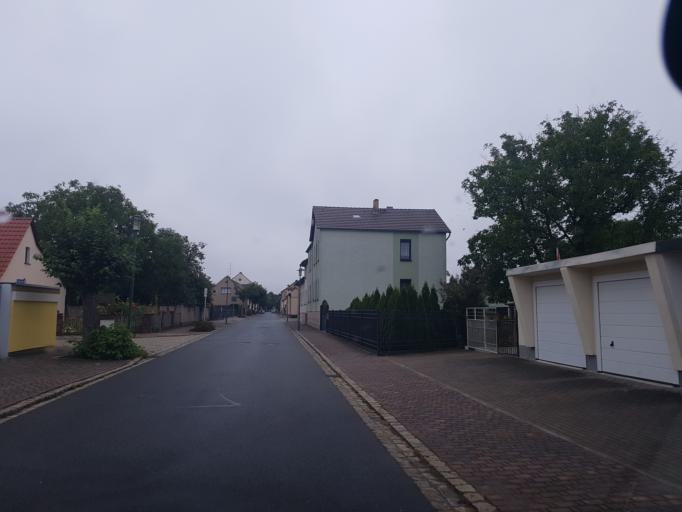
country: DE
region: Brandenburg
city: Elsterwerda
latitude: 51.4587
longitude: 13.5260
